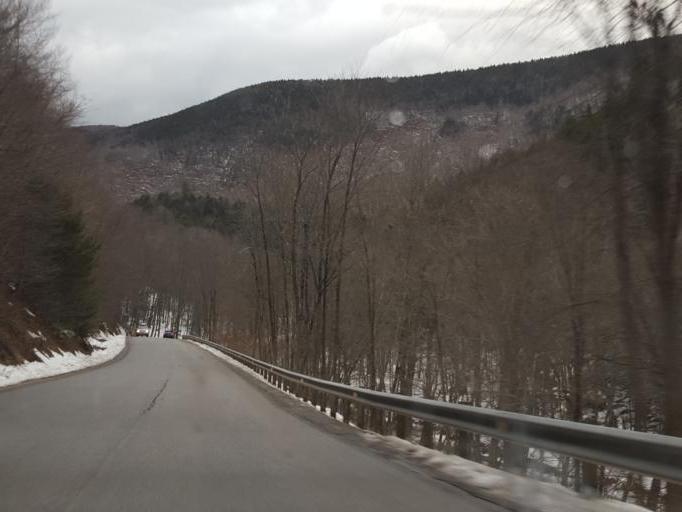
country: US
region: Vermont
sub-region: Rutland County
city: Rutland
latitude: 43.6103
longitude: -72.7568
